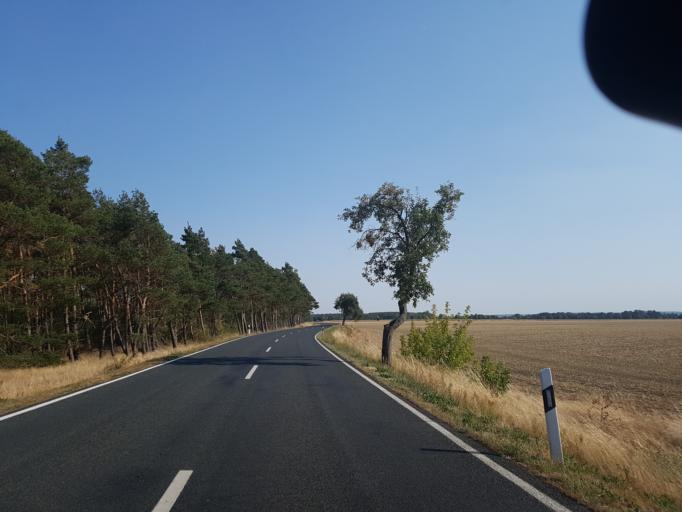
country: DE
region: Saxony
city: Beilrode
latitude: 51.5571
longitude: 13.0802
